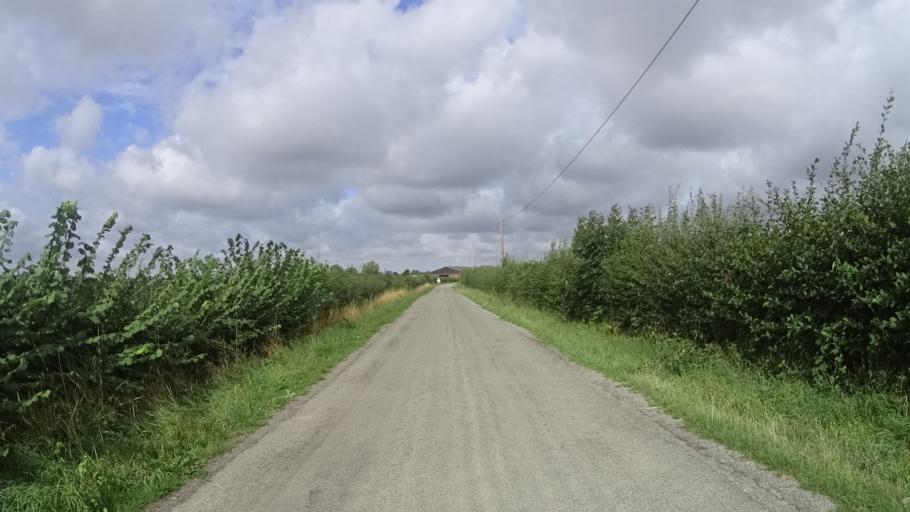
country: FR
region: Picardie
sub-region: Departement de l'Aisne
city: Boue
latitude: 50.0457
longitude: 3.6651
